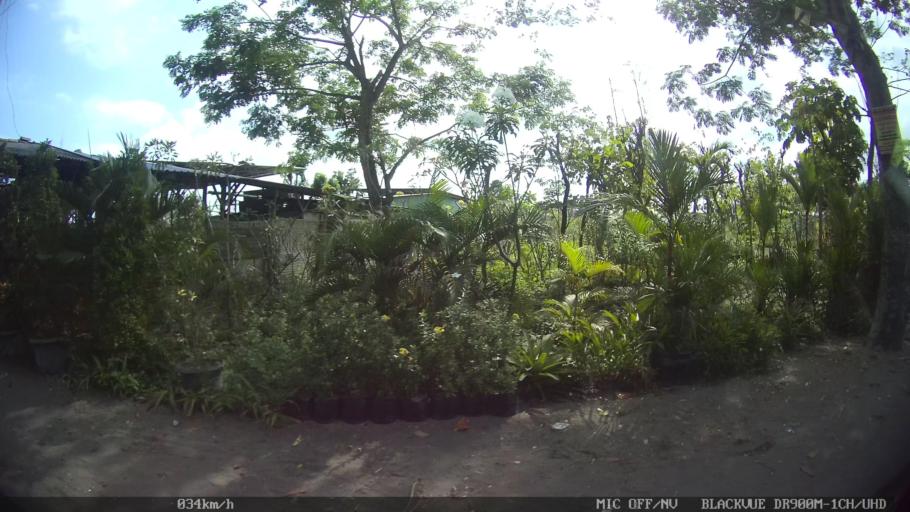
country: ID
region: Daerah Istimewa Yogyakarta
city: Depok
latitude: -7.7443
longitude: 110.4193
